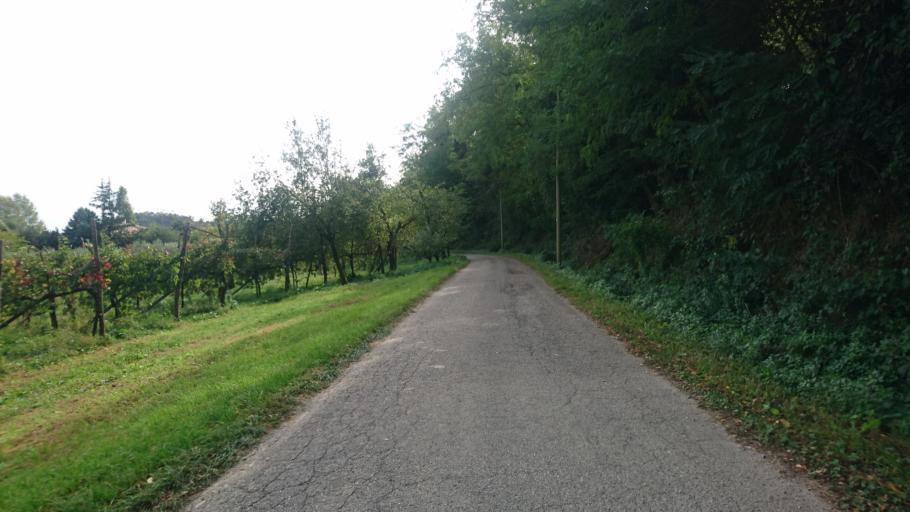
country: IT
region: Veneto
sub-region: Provincia di Padova
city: Arqua Petrarca
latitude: 45.2864
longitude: 11.7258
